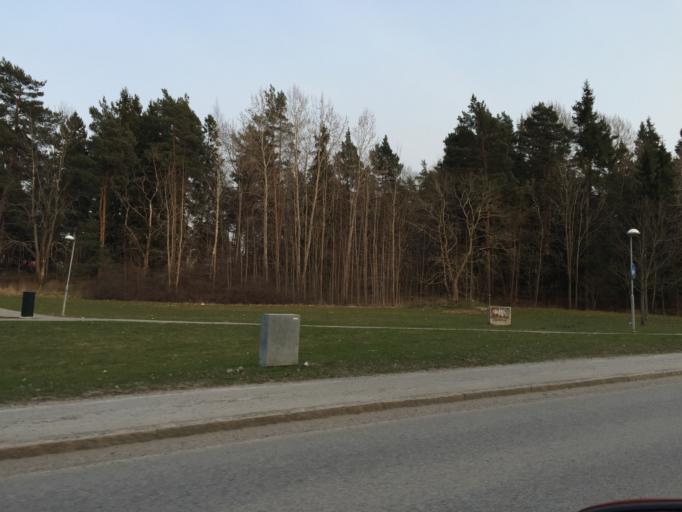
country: SE
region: Stockholm
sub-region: Stockholms Kommun
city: Bromma
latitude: 59.3538
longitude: 17.8880
